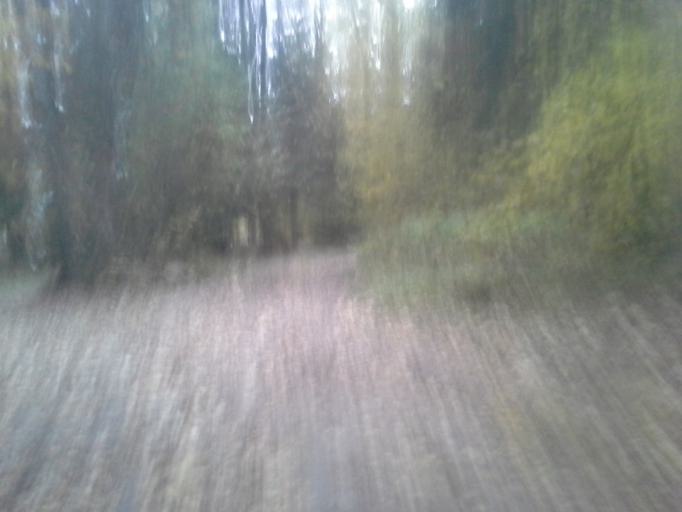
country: RU
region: Moskovskaya
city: Lesnoy Gorodok
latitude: 55.6372
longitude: 37.2463
